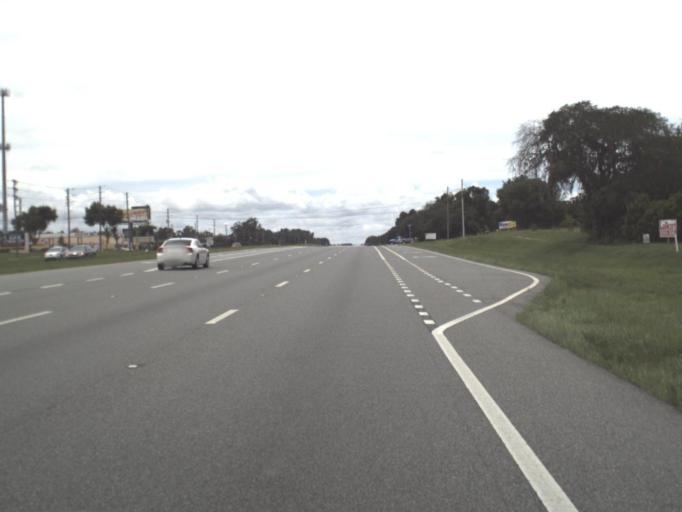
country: US
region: Florida
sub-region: Pasco County
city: Land O' Lakes
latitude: 28.1861
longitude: -82.4154
